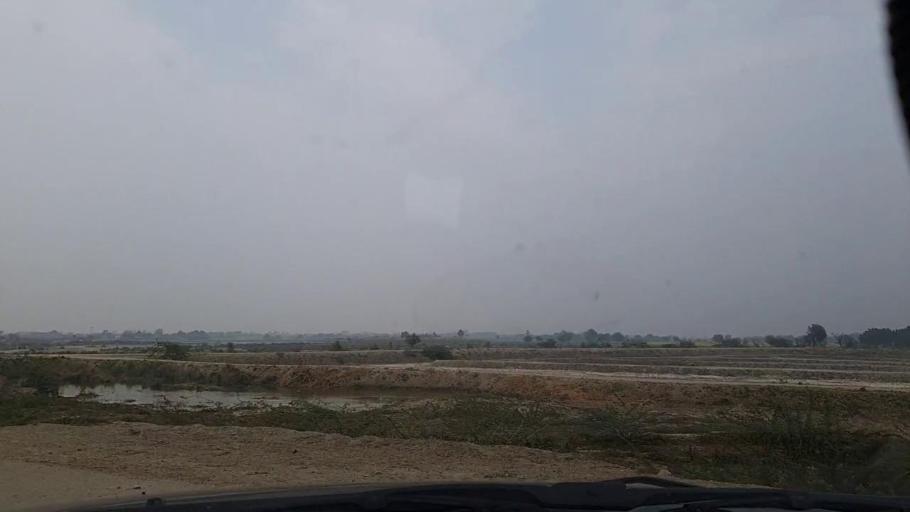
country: PK
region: Sindh
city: Tando Mittha Khan
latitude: 25.8056
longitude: 69.3760
